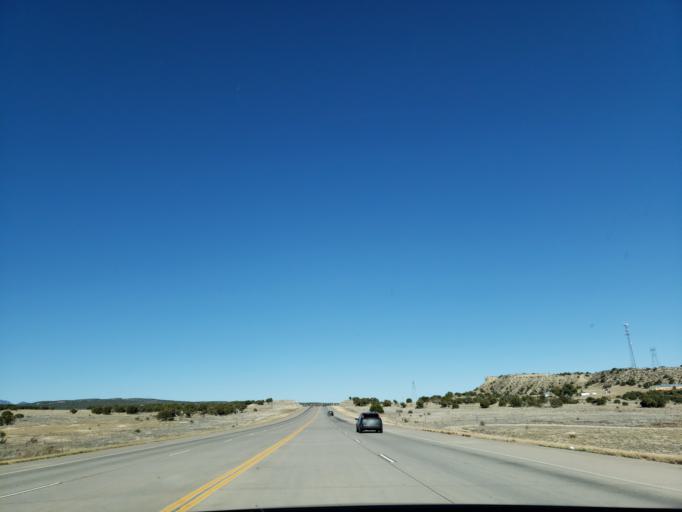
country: US
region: Colorado
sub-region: Fremont County
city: Penrose
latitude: 38.4593
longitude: -105.0071
